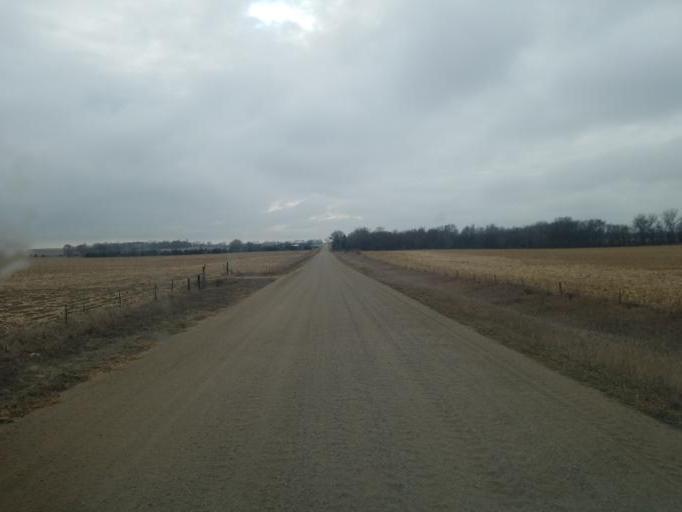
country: US
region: Nebraska
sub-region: Knox County
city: Creighton
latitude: 42.4626
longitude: -97.7984
